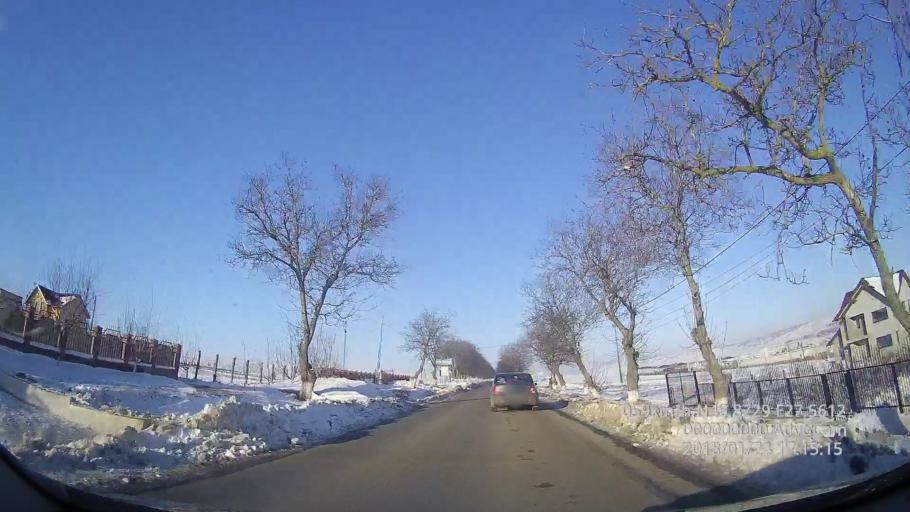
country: RO
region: Vaslui
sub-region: Comuna Rebricea
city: Rebricea
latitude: 46.8735
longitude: 27.5614
